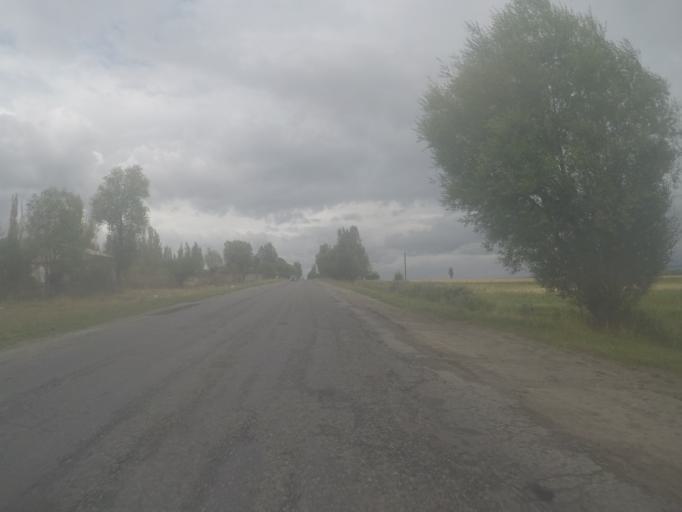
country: KG
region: Ysyk-Koel
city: Tyup
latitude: 42.7475
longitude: 78.0940
